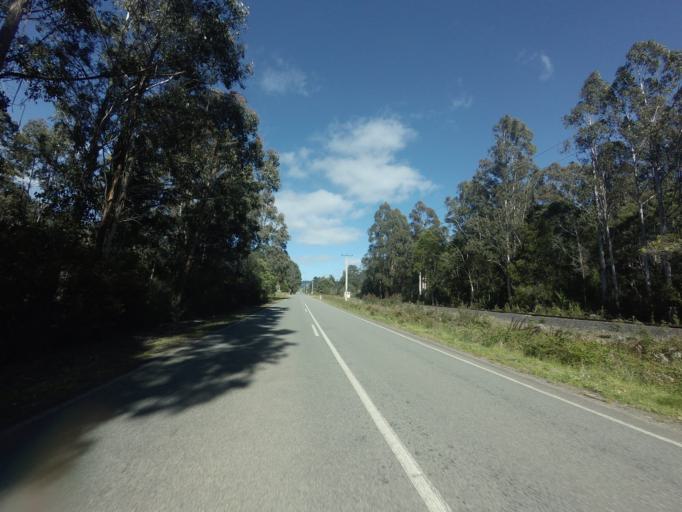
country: AU
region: Tasmania
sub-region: Derwent Valley
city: New Norfolk
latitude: -42.7172
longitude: 146.6898
